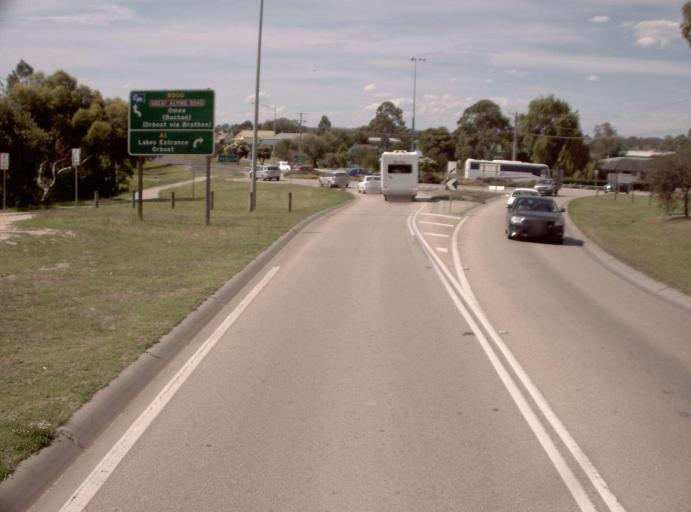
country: AU
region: Victoria
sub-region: East Gippsland
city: Bairnsdale
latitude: -37.8198
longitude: 147.6490
